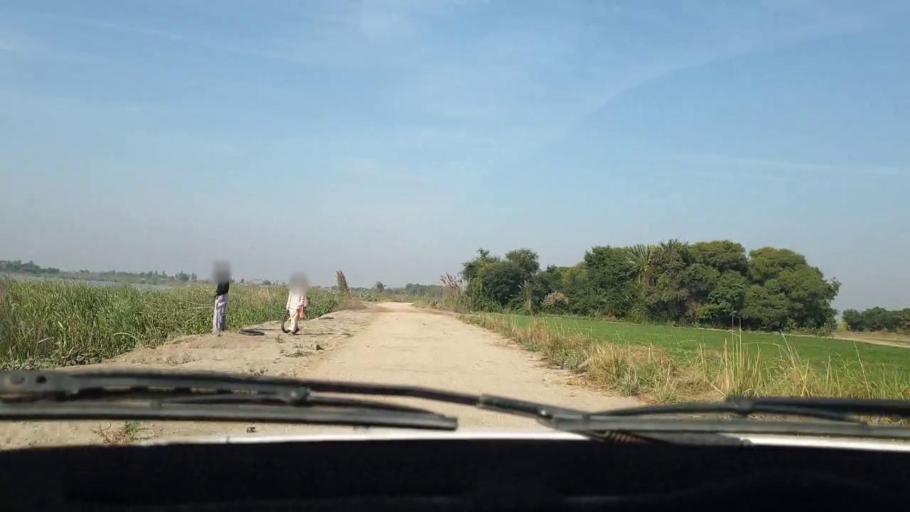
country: PK
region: Sindh
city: Tando Muhammad Khan
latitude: 25.0004
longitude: 68.4607
